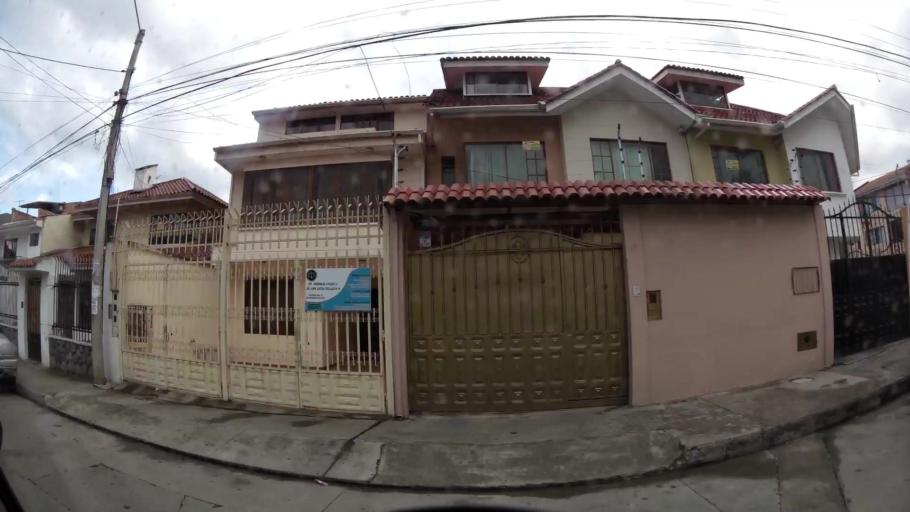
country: EC
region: Azuay
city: Cuenca
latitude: -2.8994
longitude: -79.0240
